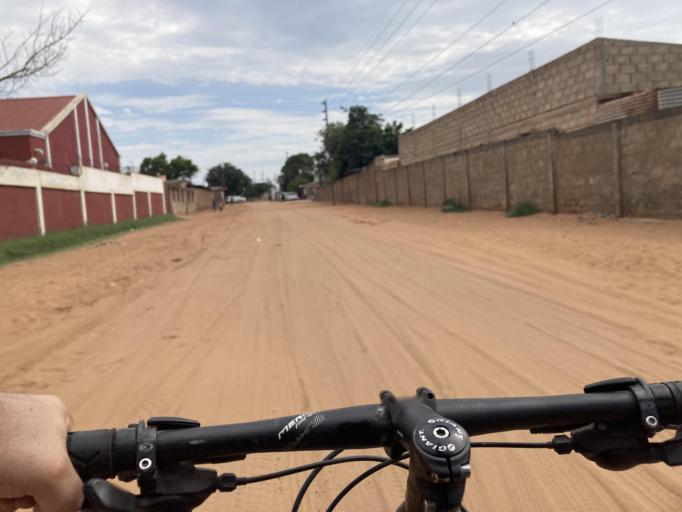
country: MZ
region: Maputo City
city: Maputo
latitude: -25.8948
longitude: 32.6074
